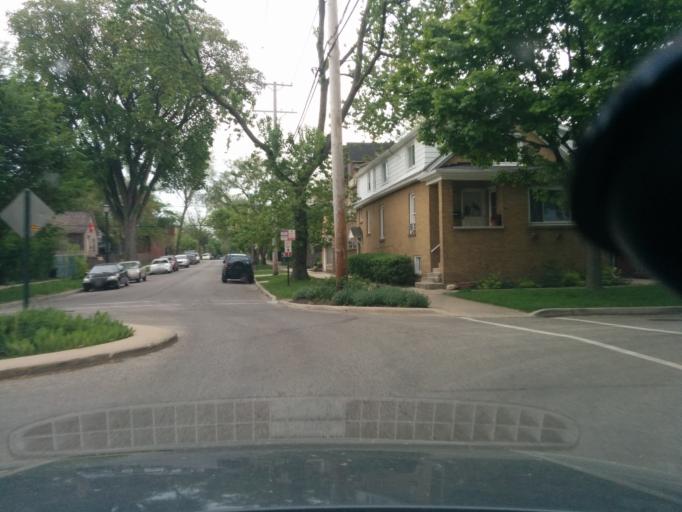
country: US
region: Illinois
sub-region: Cook County
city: Evanston
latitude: 42.0376
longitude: -87.6963
